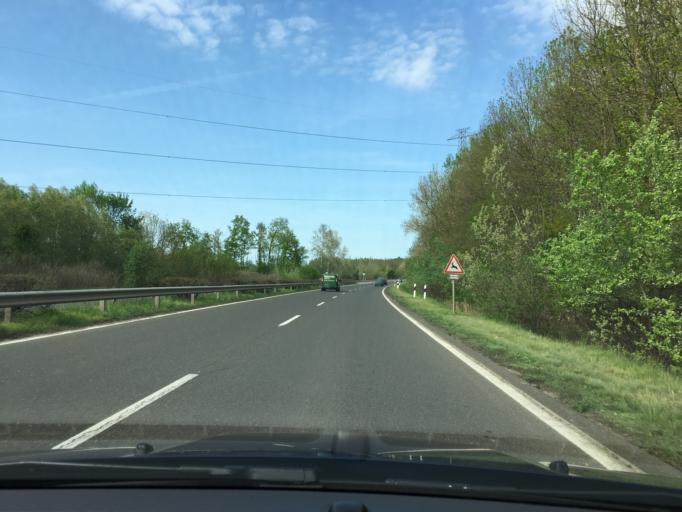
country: HU
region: Csongrad
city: Algyo
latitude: 46.3592
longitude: 20.2080
